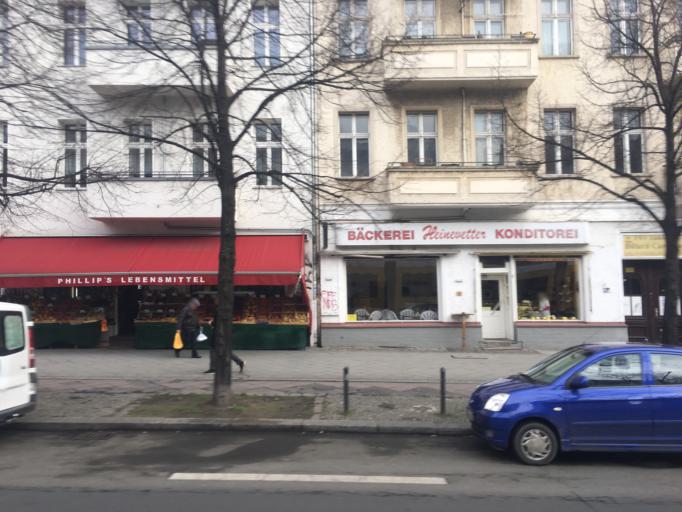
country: DE
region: Berlin
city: Friedrichshain Bezirk
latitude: 52.5176
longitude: 13.4537
